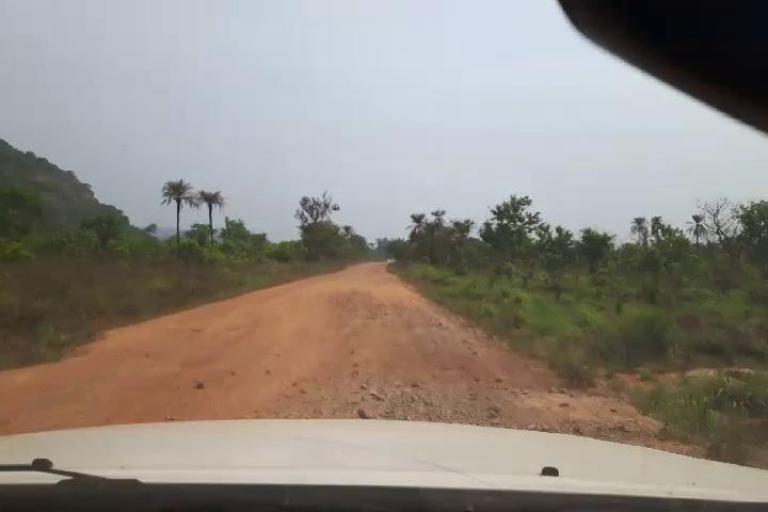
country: SL
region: Northern Province
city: Masingbi
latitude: 8.8855
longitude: -11.8191
